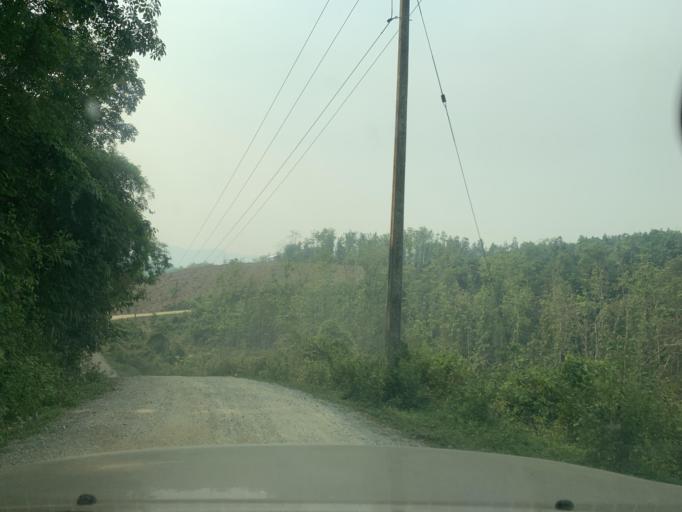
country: LA
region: Louangphabang
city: Louangphabang
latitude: 19.8897
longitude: 102.2516
